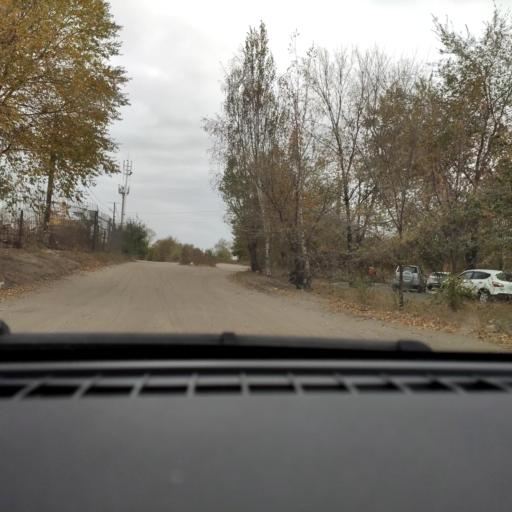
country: RU
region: Voronezj
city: Voronezh
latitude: 51.6636
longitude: 39.2874
